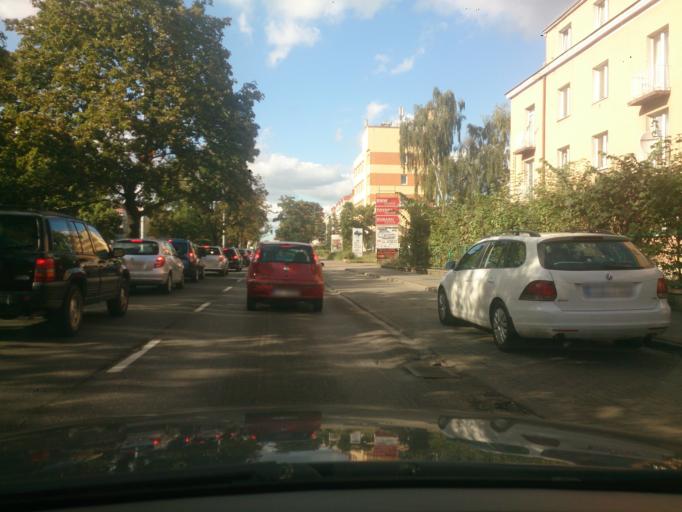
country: PL
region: Pomeranian Voivodeship
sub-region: Sopot
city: Sopot
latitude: 54.4258
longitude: 18.5632
